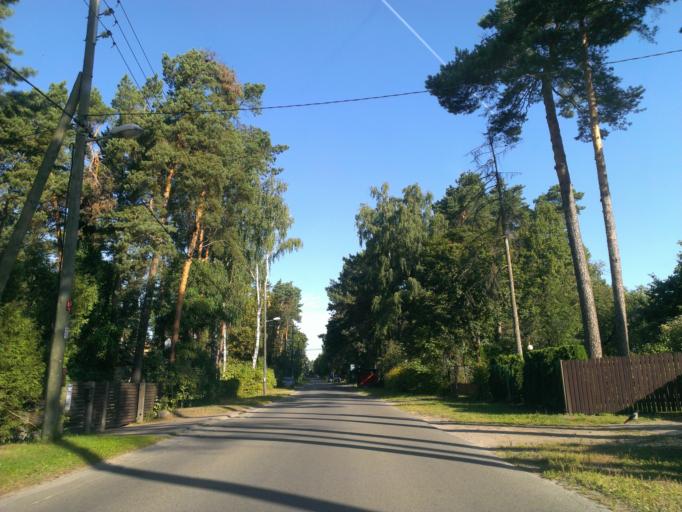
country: LV
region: Riga
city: Bergi
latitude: 56.9826
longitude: 24.3012
